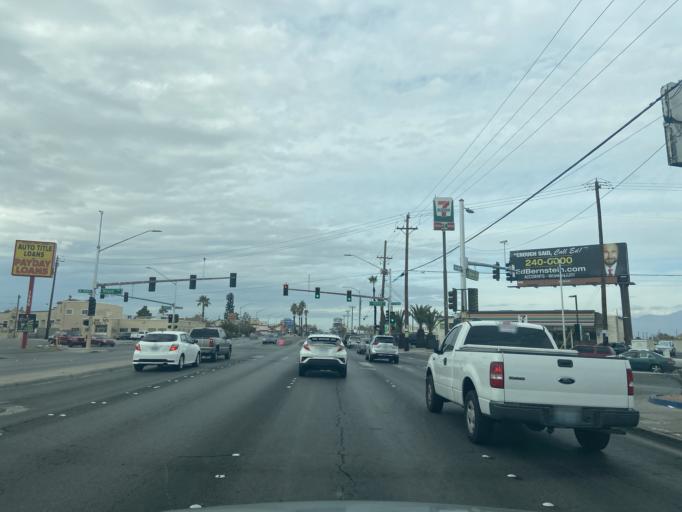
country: US
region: Nevada
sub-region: Clark County
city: Las Vegas
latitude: 36.1881
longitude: -115.1855
